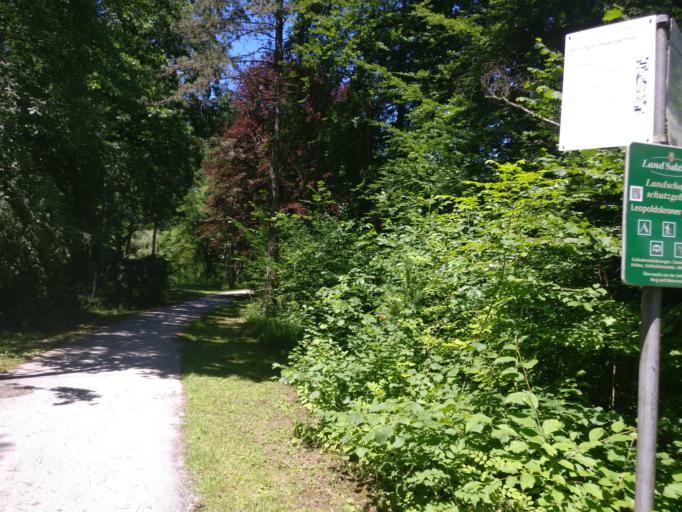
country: AT
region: Salzburg
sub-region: Salzburg Stadt
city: Salzburg
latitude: 47.7879
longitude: 13.0459
